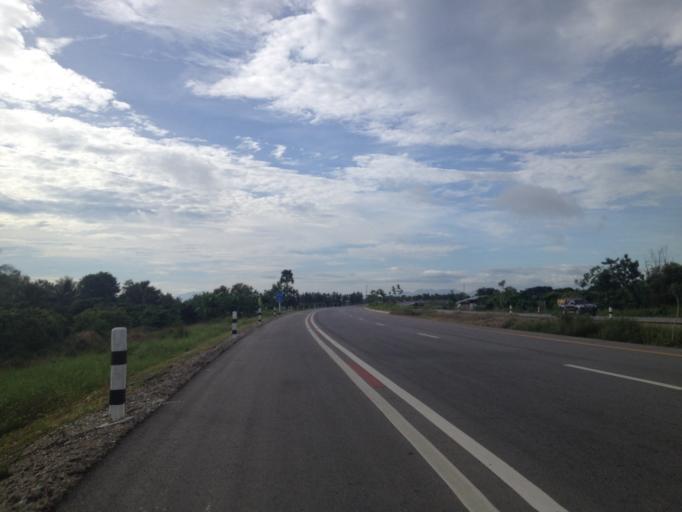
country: TH
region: Chiang Mai
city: San Pa Tong
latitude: 18.5675
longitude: 98.8494
